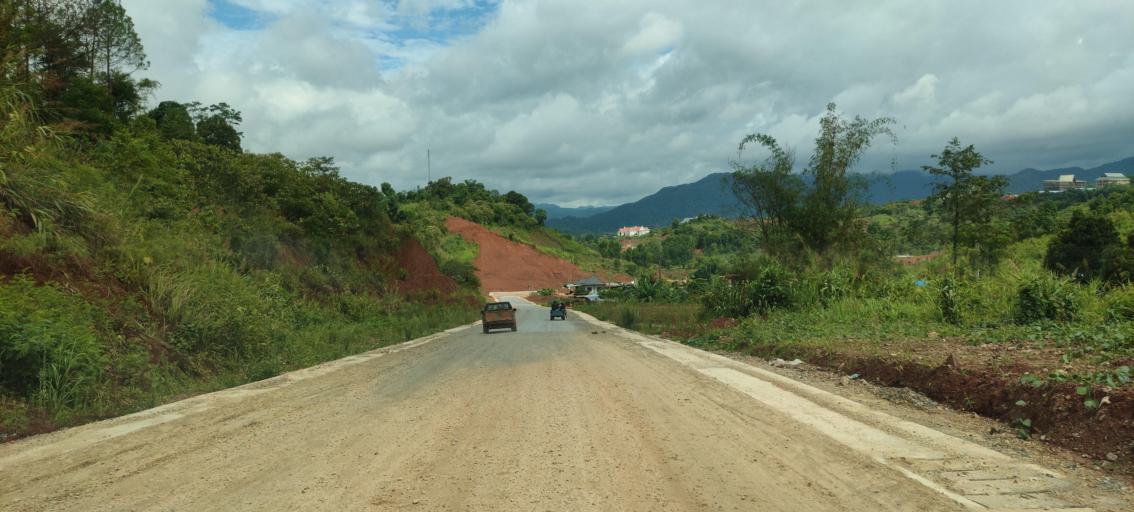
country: LA
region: Phongsali
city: Phongsali
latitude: 21.6338
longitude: 101.9229
